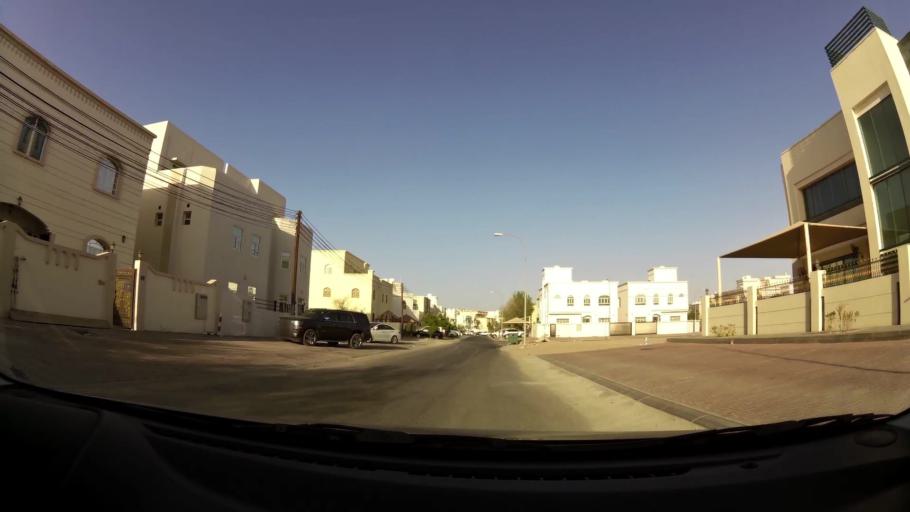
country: OM
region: Muhafazat Masqat
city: As Sib al Jadidah
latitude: 23.6136
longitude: 58.2181
